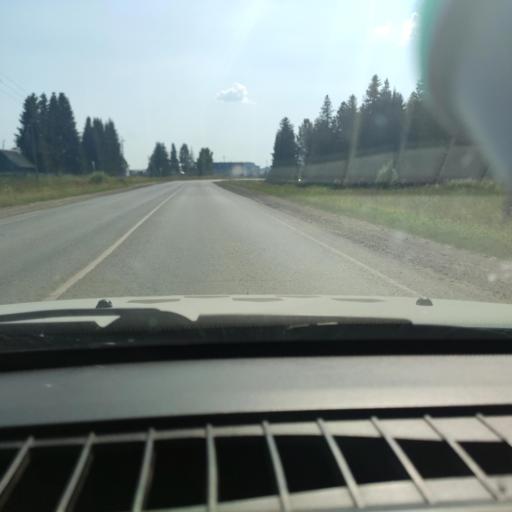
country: RU
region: Perm
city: Orda
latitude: 57.2013
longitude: 56.9196
